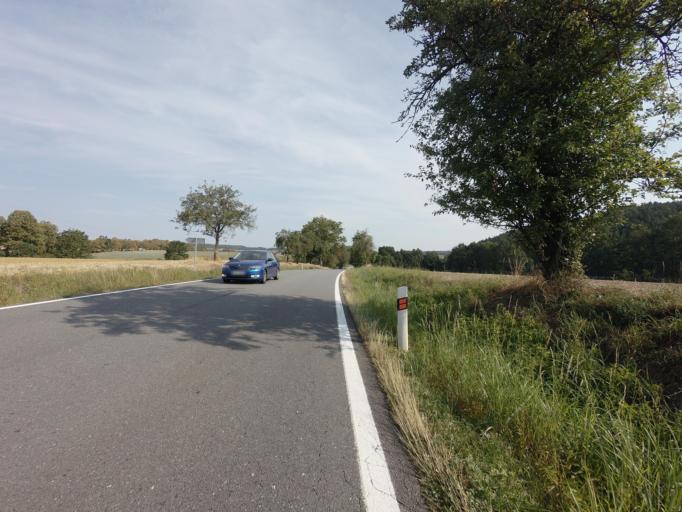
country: CZ
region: Jihocesky
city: Milevsko
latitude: 49.4682
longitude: 14.3614
